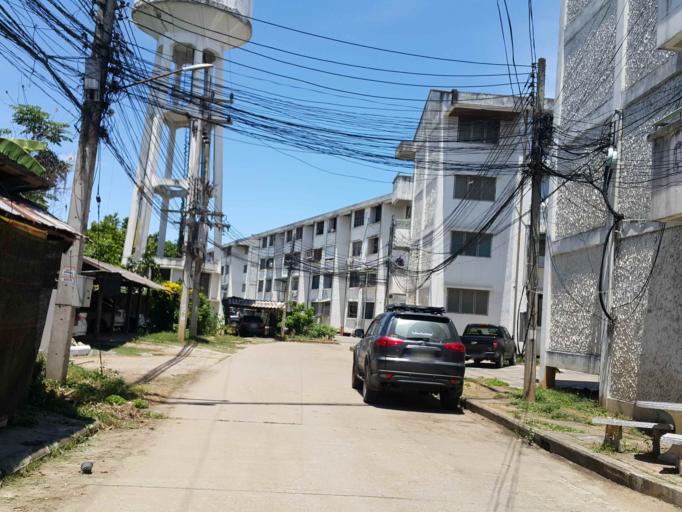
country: TH
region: Chiang Mai
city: Chiang Mai
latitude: 18.7585
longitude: 98.9972
